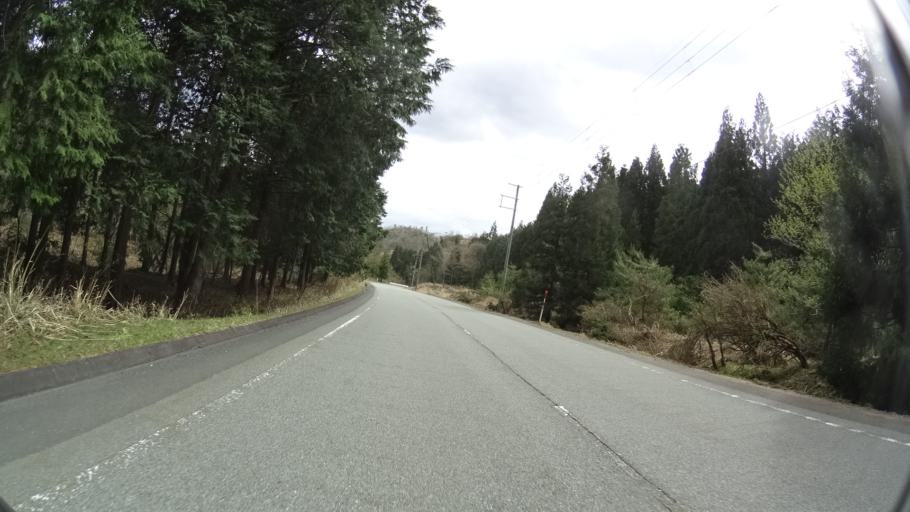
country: JP
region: Hyogo
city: Toyooka
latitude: 35.4923
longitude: 134.9179
